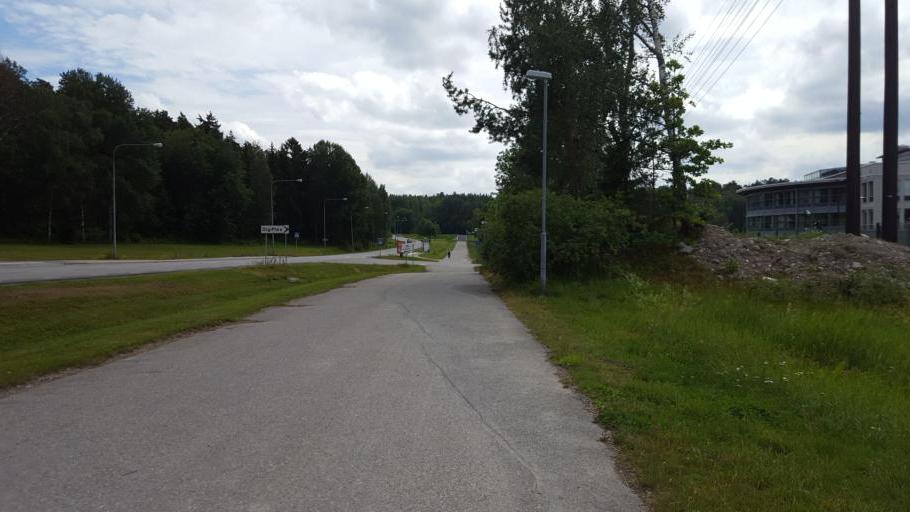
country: SE
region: Stockholm
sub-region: Upplands Vasby Kommun
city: Upplands Vaesby
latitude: 59.5104
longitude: 17.8997
